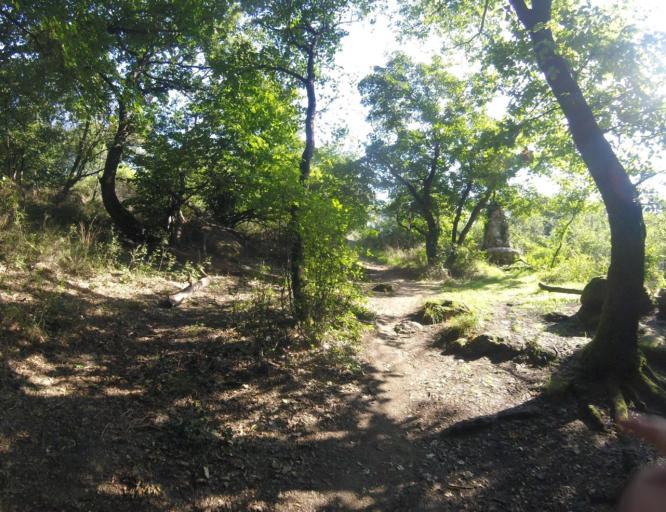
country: HU
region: Fejer
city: Lovasbereny
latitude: 47.2553
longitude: 18.5779
